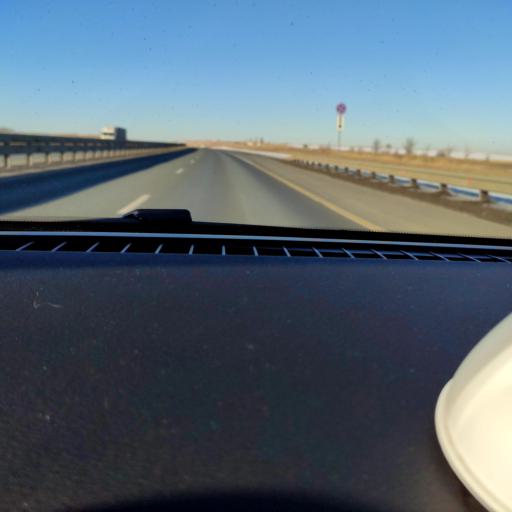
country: RU
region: Samara
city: Smyshlyayevka
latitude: 53.1448
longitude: 50.4101
